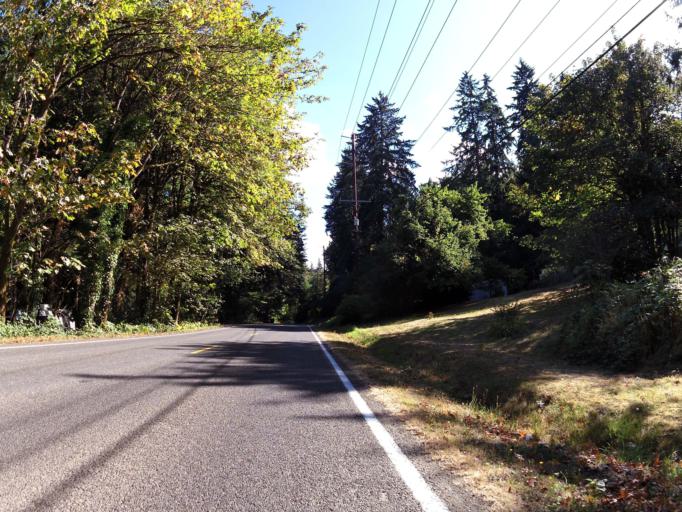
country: US
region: Washington
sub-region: Thurston County
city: Olympia
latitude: 47.0602
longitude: -123.0133
